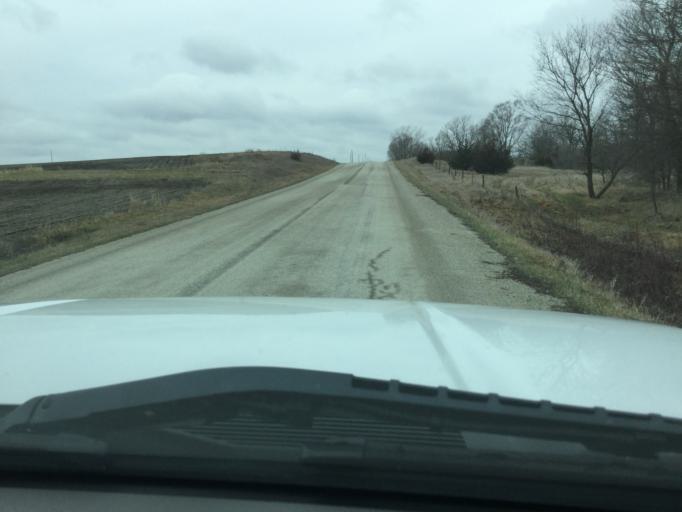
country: US
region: Kansas
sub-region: Nemaha County
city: Sabetha
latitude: 39.7979
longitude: -95.7485
